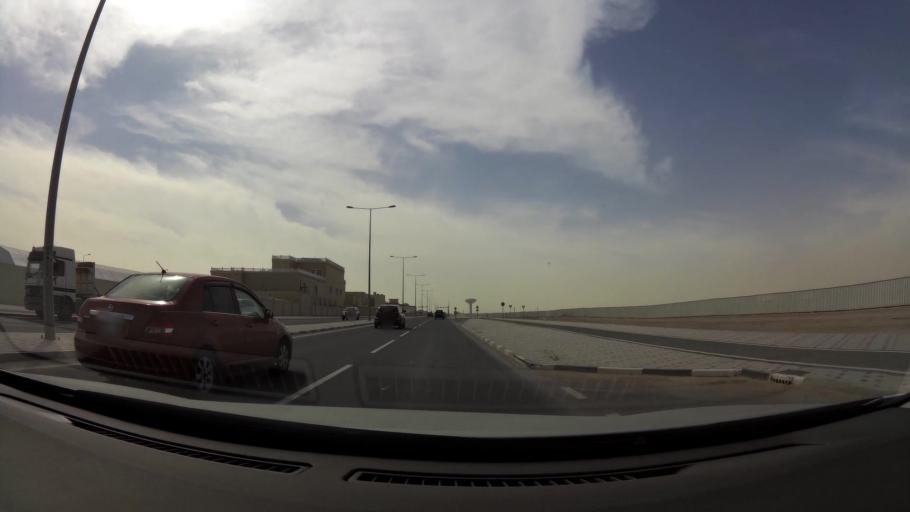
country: QA
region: Baladiyat ar Rayyan
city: Ar Rayyan
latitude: 25.3171
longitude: 51.4132
